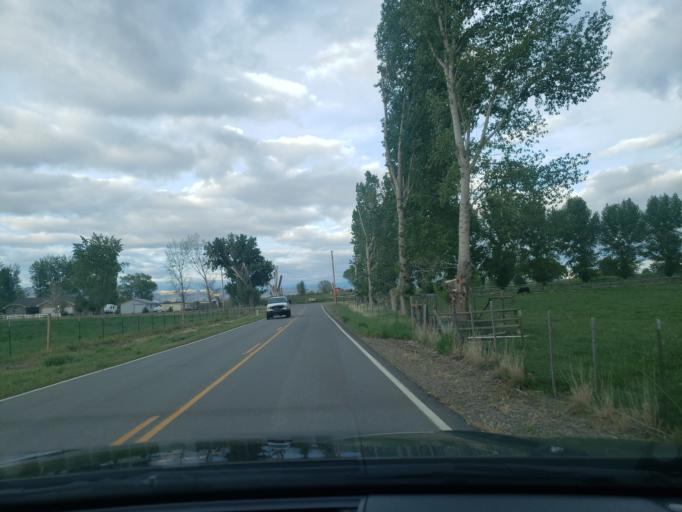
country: US
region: Colorado
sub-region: Mesa County
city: Fruita
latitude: 39.2112
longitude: -108.7211
